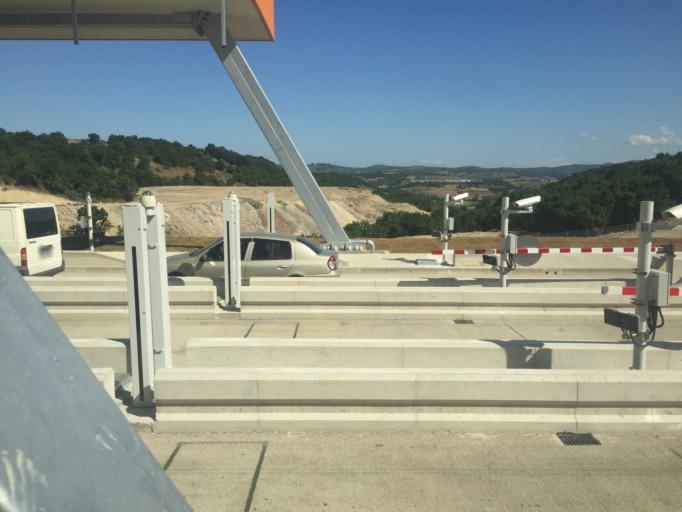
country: TR
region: Bursa
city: Mahmudiye
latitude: 40.2566
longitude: 28.7099
